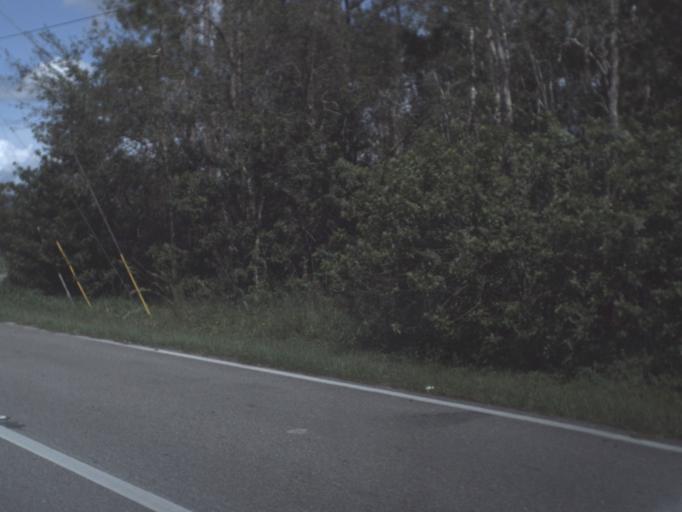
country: US
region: Florida
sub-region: Lee County
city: Fort Myers
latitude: 26.5943
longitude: -81.8503
